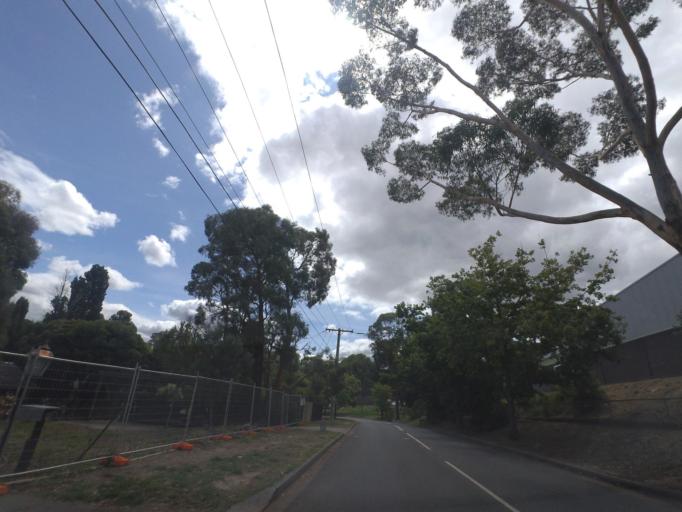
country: AU
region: Victoria
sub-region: Manningham
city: Park Orchards
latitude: -37.7798
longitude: 145.2144
